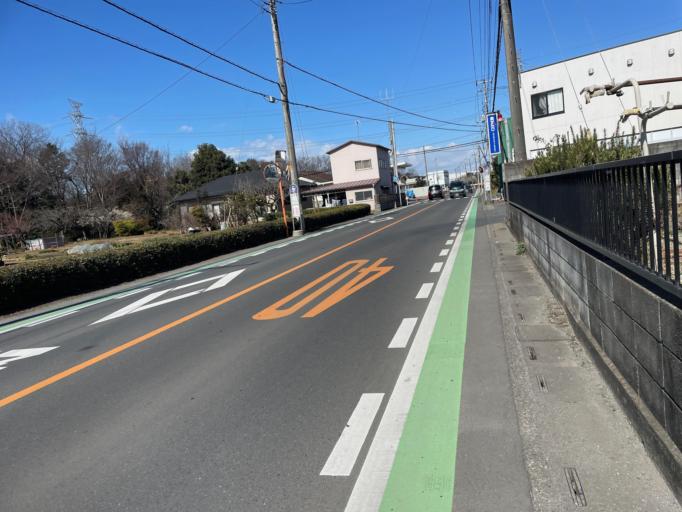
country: JP
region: Saitama
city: Sakado
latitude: 35.9549
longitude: 139.4329
